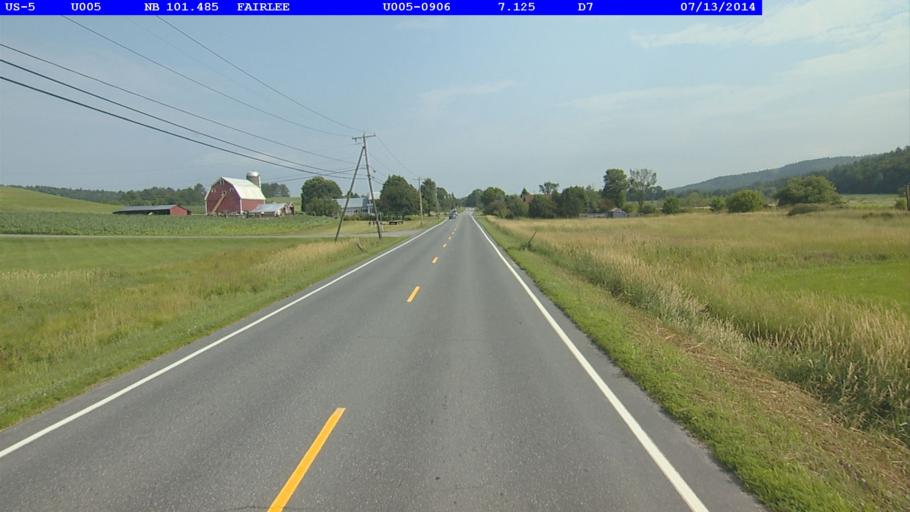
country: US
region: New Hampshire
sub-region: Grafton County
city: Orford
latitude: 43.9592
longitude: -72.1153
